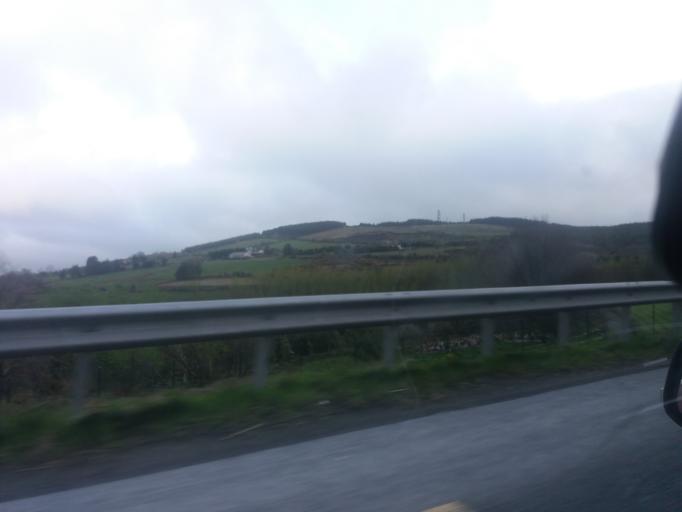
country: IE
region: Munster
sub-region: County Limerick
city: Newcastle West
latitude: 52.4217
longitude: -9.1311
